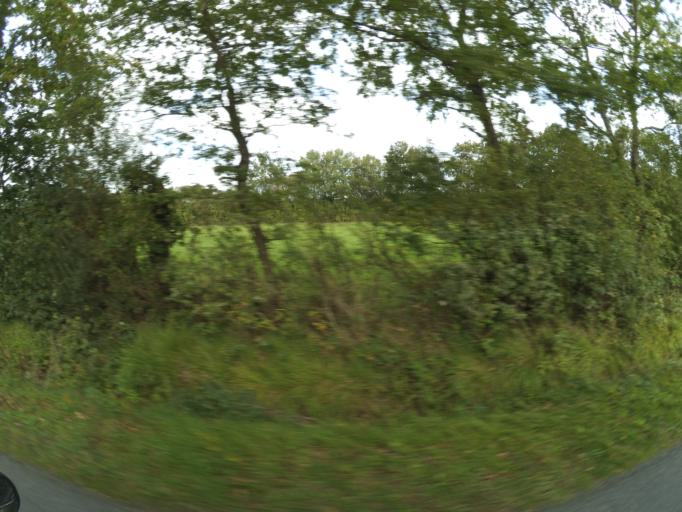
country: FR
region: Pays de la Loire
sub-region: Departement de la Loire-Atlantique
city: Bouvron
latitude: 47.4545
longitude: -1.8248
